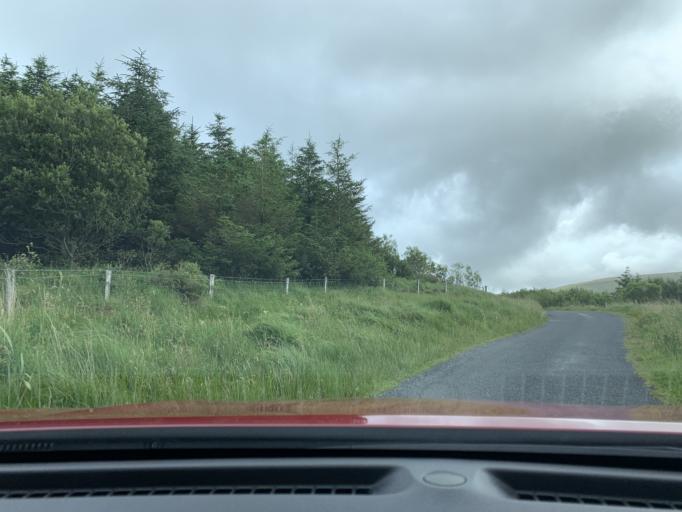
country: IE
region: Connaught
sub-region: Sligo
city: Sligo
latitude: 54.3805
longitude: -8.4130
